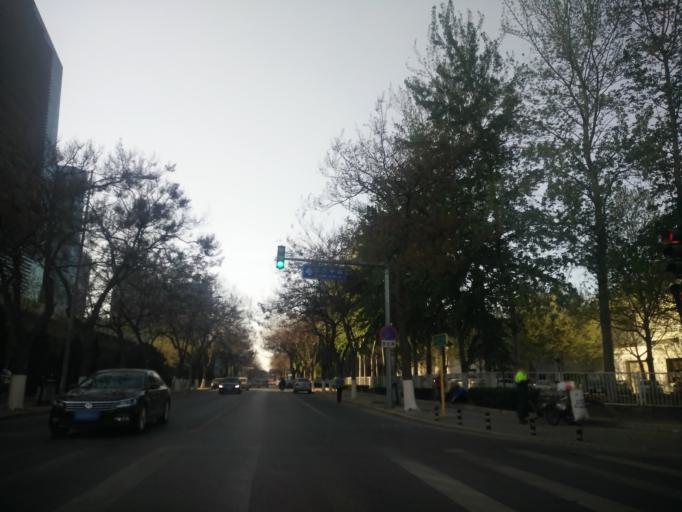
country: CN
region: Beijing
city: Jiugong
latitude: 39.7913
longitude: 116.5084
